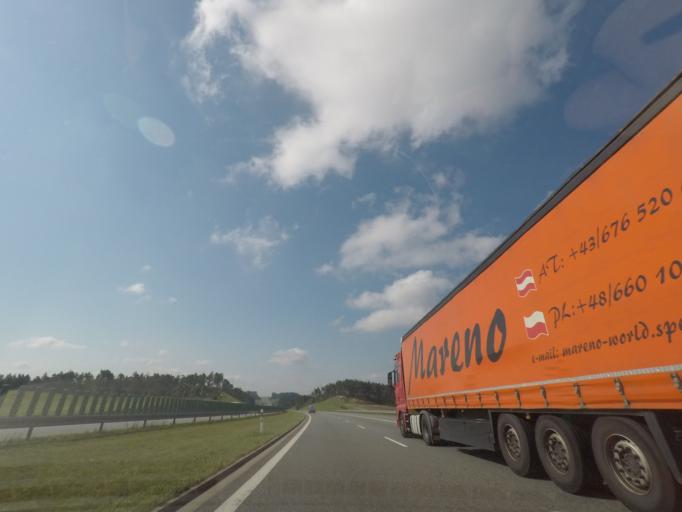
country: PL
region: Pomeranian Voivodeship
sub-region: Powiat tczewski
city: Tczew
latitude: 54.0648
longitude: 18.6719
